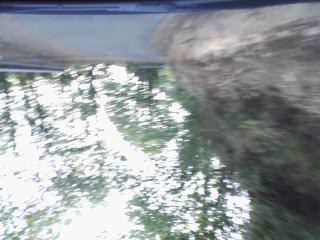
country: IT
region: Calabria
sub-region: Provincia di Vibo-Valentia
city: Nardodipace
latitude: 38.4450
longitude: 16.3394
